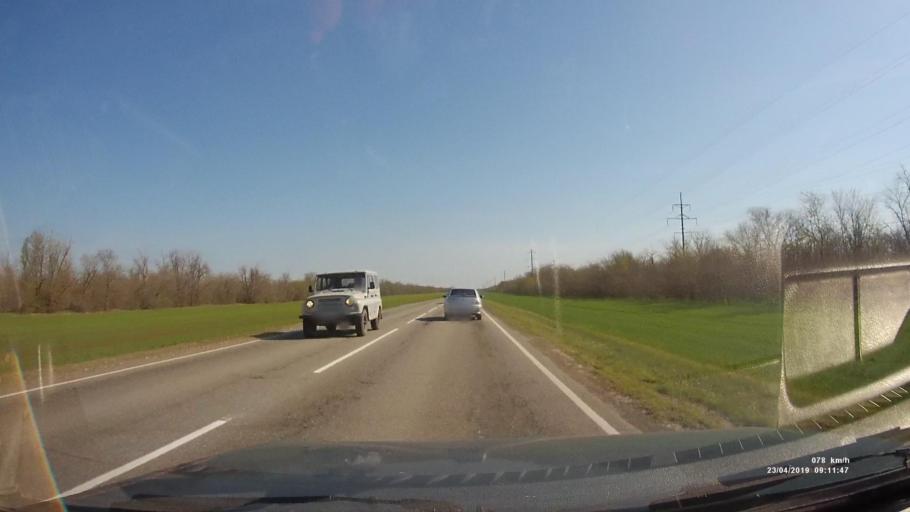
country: RU
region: Rostov
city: Proletarsk
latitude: 46.5994
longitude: 41.6329
